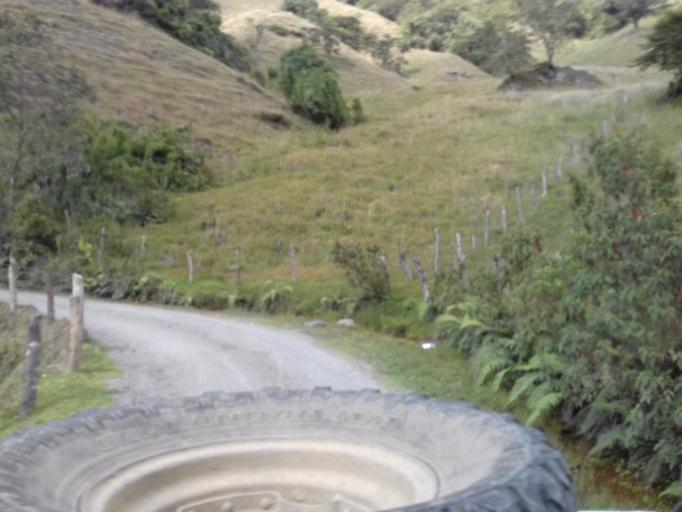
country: CO
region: Quindio
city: Salento
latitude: 4.5528
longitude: -75.4987
